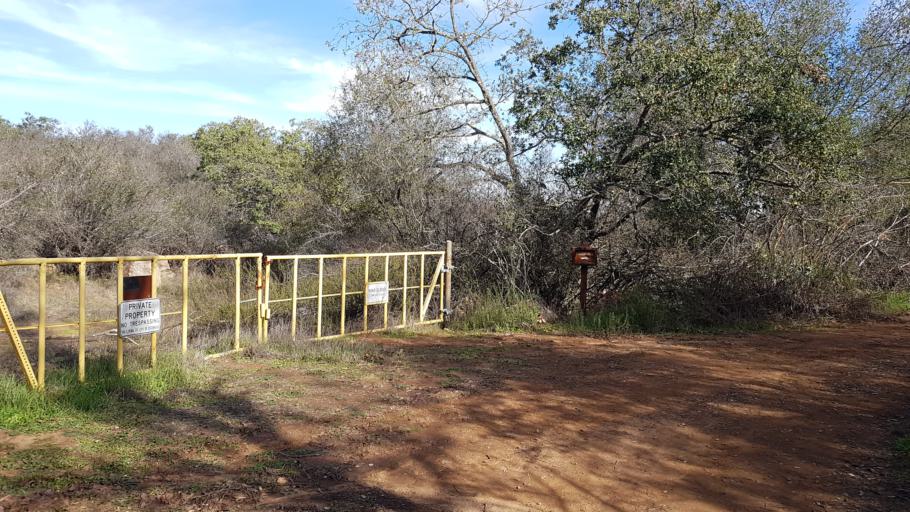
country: US
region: California
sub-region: San Diego County
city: Valley Center
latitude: 33.1821
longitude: -117.0340
